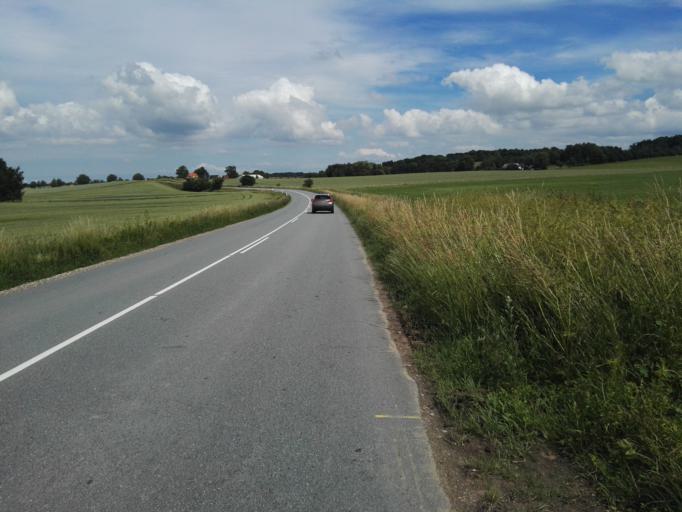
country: DK
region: Capital Region
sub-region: Frederikssund Kommune
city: Slangerup
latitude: 55.8601
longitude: 12.1763
